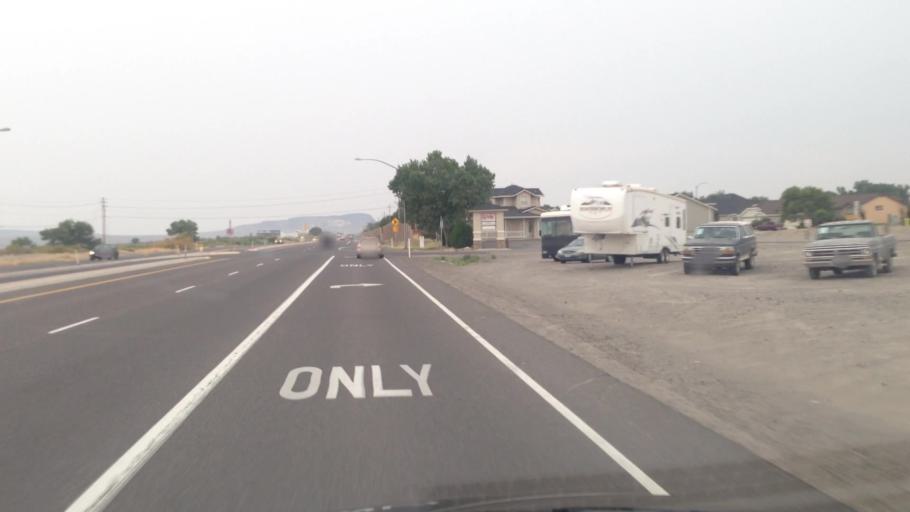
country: US
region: Nevada
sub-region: Lyon County
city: Fernley
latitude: 39.5927
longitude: -119.1560
